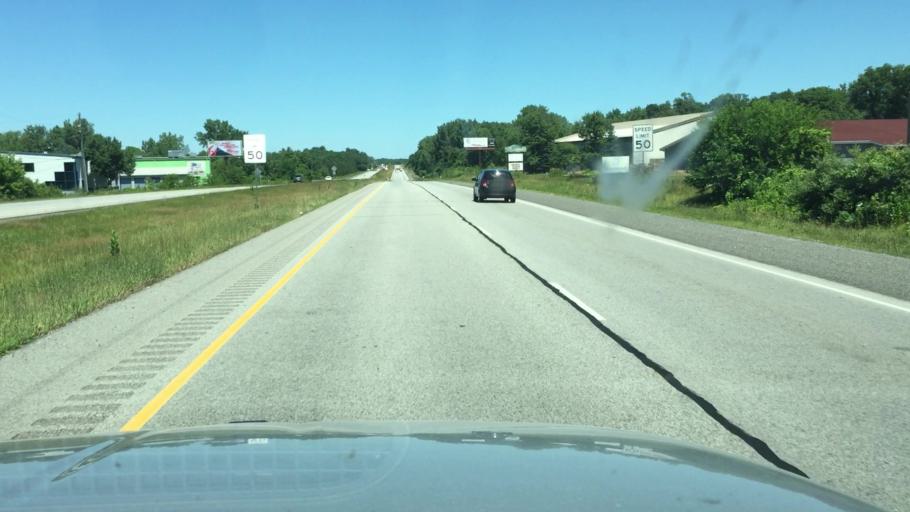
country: US
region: Indiana
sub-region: Porter County
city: Chesterton
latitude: 41.5952
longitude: -87.0452
